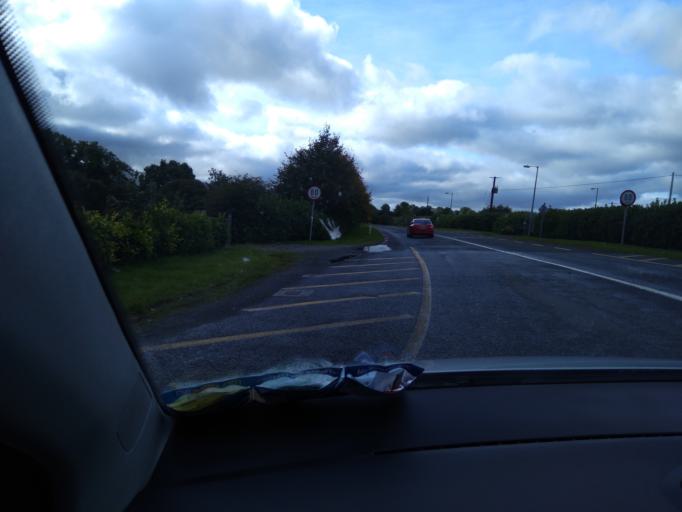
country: IE
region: Connaught
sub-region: Sligo
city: Collooney
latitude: 54.1904
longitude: -8.4461
